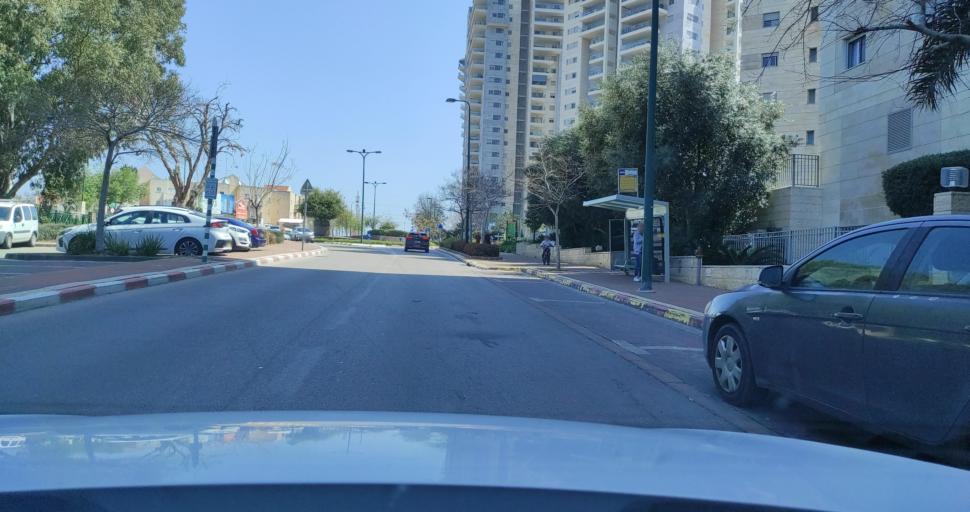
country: IL
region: Central District
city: Nordiyya
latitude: 32.3025
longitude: 34.8792
